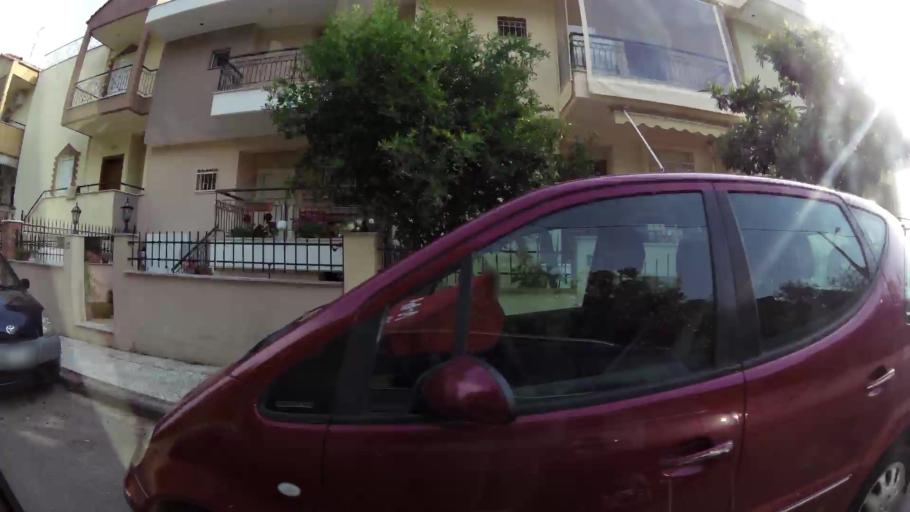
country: GR
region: Central Macedonia
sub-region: Nomos Thessalonikis
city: Oraiokastro
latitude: 40.7217
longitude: 22.9137
